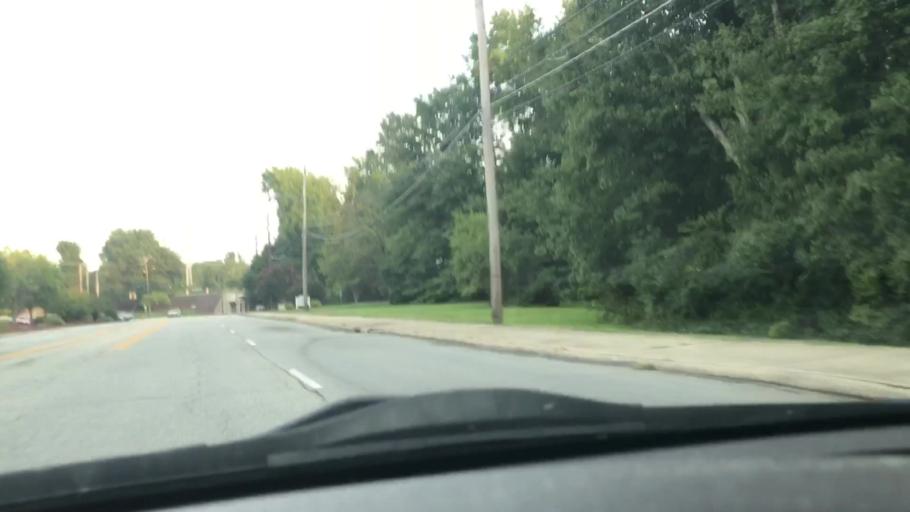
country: US
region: North Carolina
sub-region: Guilford County
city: Greensboro
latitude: 36.0836
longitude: -79.8328
